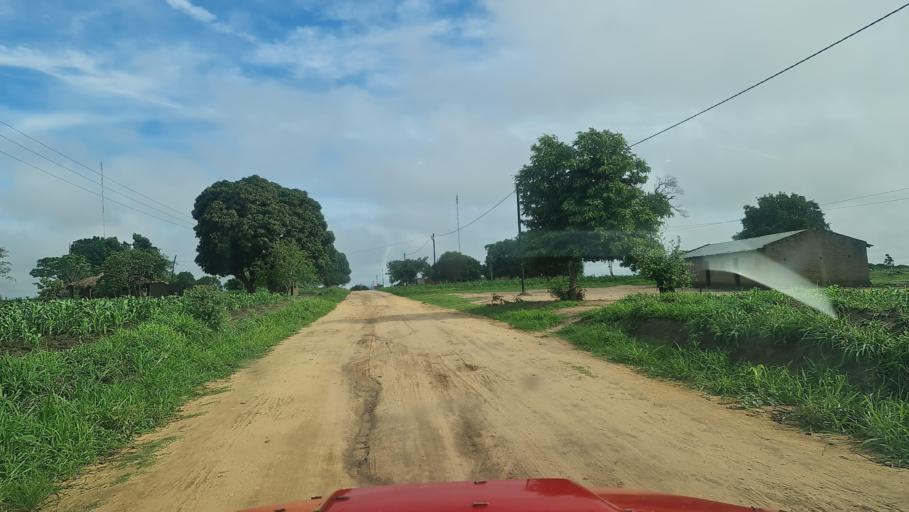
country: MW
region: Southern Region
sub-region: Nsanje District
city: Nsanje
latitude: -17.3008
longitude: 35.5936
